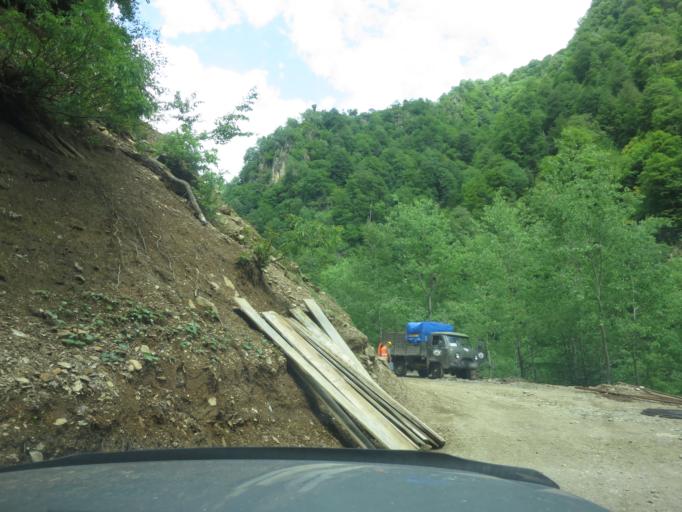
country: GE
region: Kakheti
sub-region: Telavi
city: Telavi
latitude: 42.2259
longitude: 45.4798
